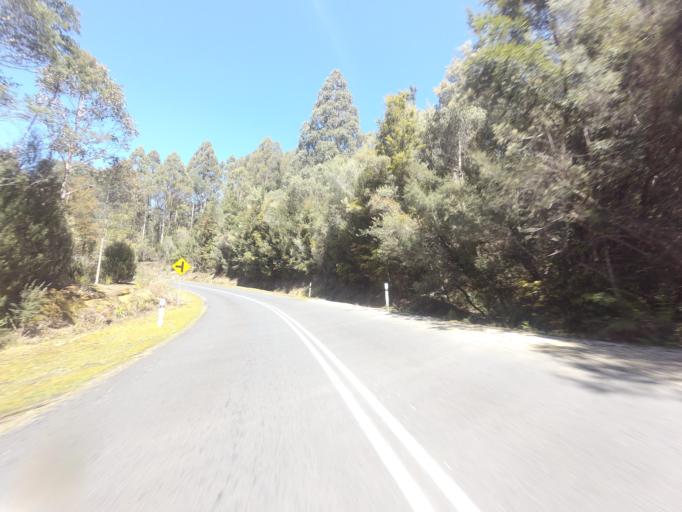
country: AU
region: Tasmania
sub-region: Huon Valley
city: Geeveston
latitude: -42.8192
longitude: 146.3317
